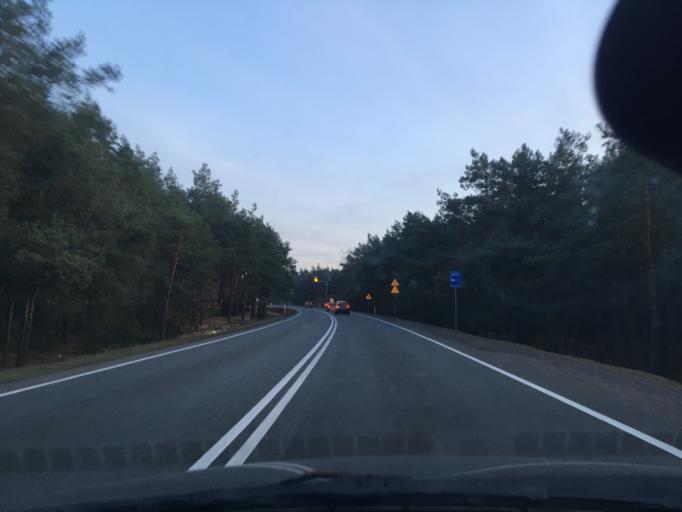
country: PL
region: Masovian Voivodeship
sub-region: Powiat plocki
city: Wyszogrod
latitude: 52.3640
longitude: 20.1946
